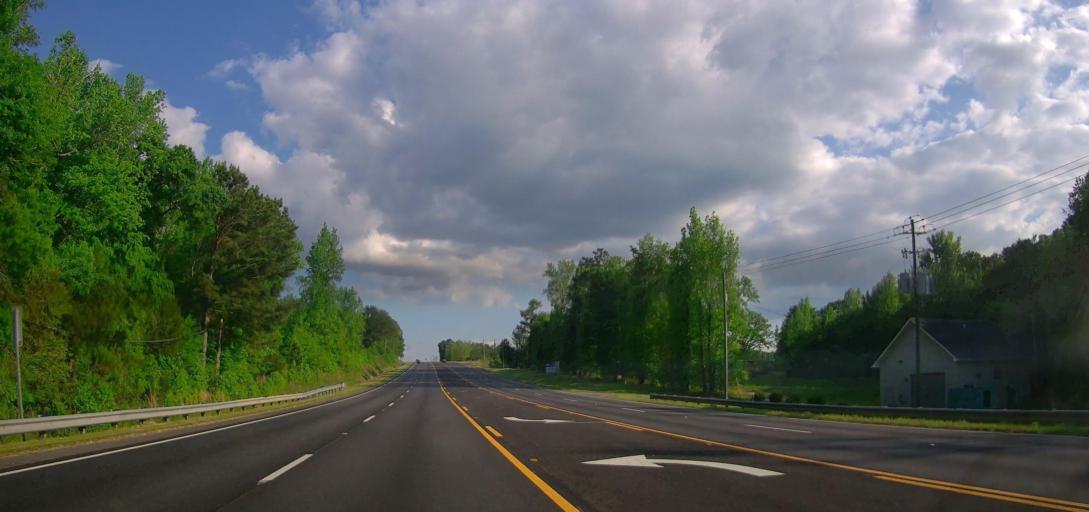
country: US
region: Georgia
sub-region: Baldwin County
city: Milledgeville
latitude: 33.1612
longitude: -83.2781
